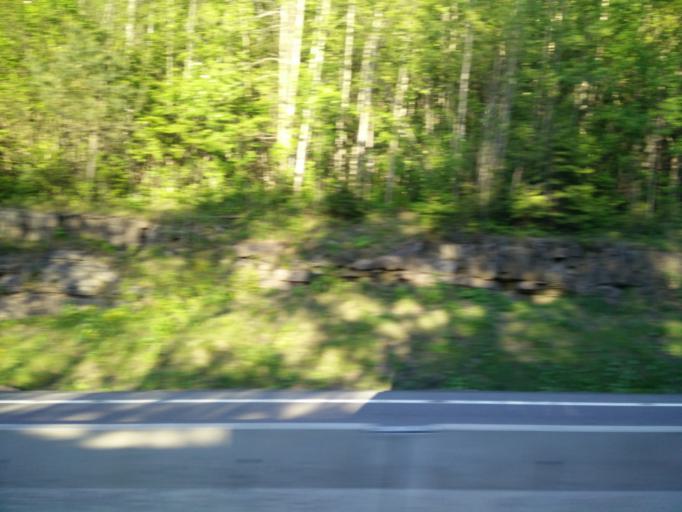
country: NO
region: Buskerud
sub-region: Hole
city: Vik
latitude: 60.0417
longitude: 10.2750
